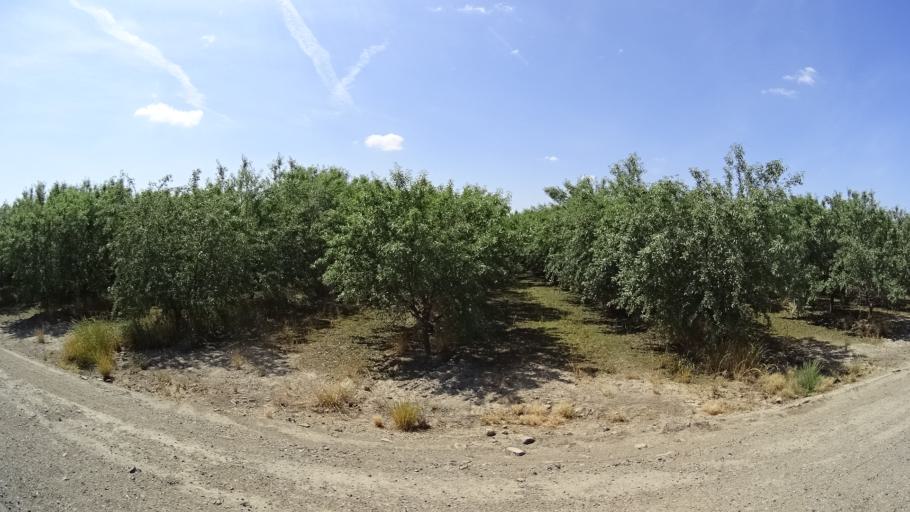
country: US
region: California
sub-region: Kings County
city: Home Garden
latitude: 36.2695
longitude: -119.5705
